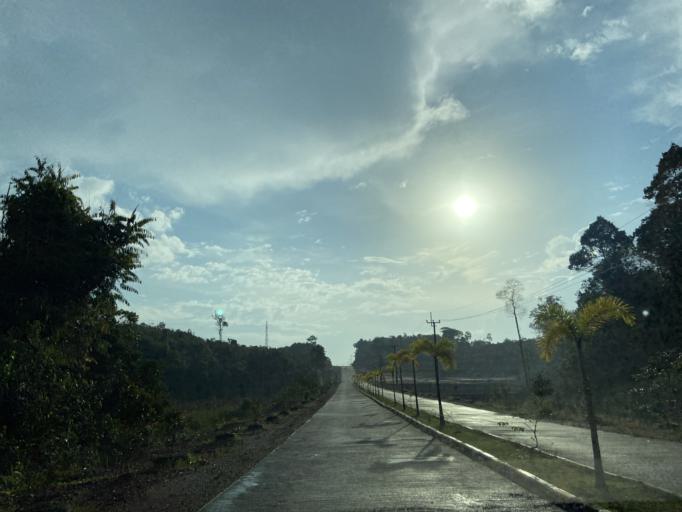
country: ID
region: Riau Islands
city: Tanjungpinang
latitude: 0.8954
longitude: 104.1247
